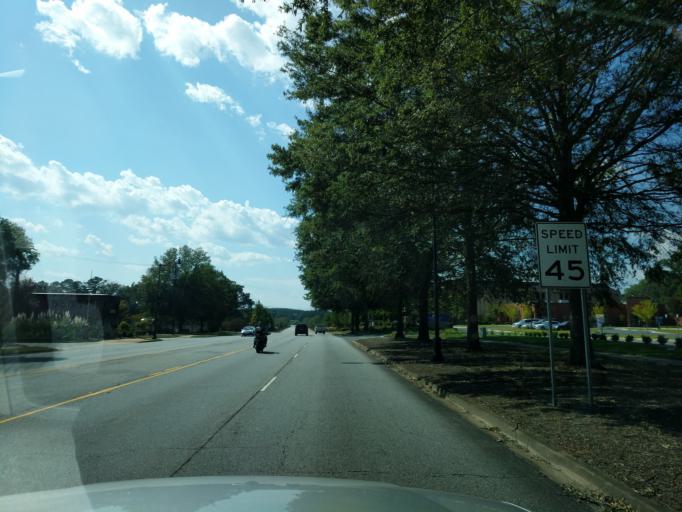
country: US
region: South Carolina
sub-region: Pickens County
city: Clemson
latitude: 34.6926
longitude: -82.8458
